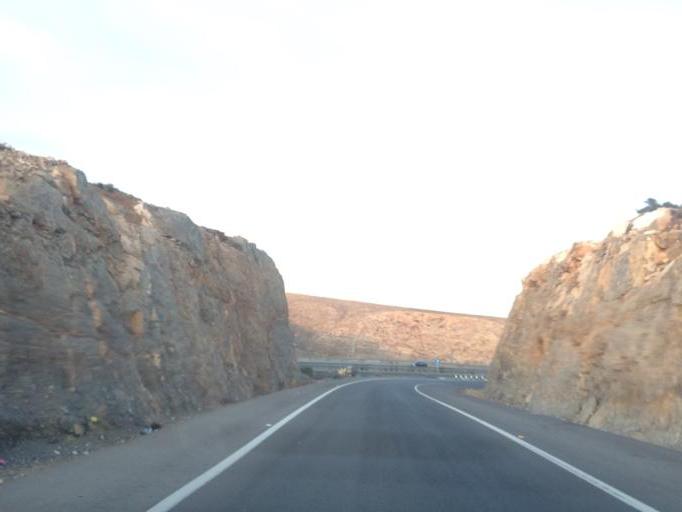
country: ES
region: Andalusia
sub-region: Provincia de Almeria
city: Almeria
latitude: 36.8308
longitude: -2.5020
